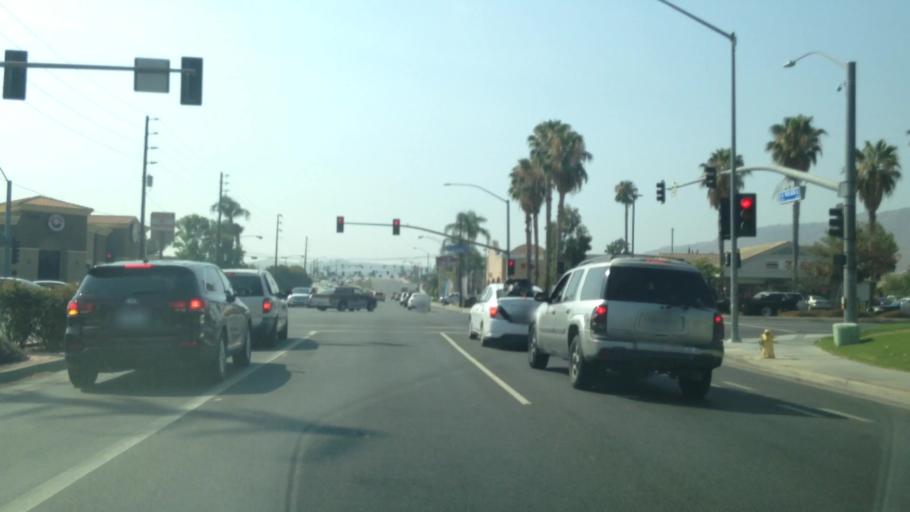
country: US
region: California
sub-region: Riverside County
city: Home Gardens
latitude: 33.9039
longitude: -117.4766
